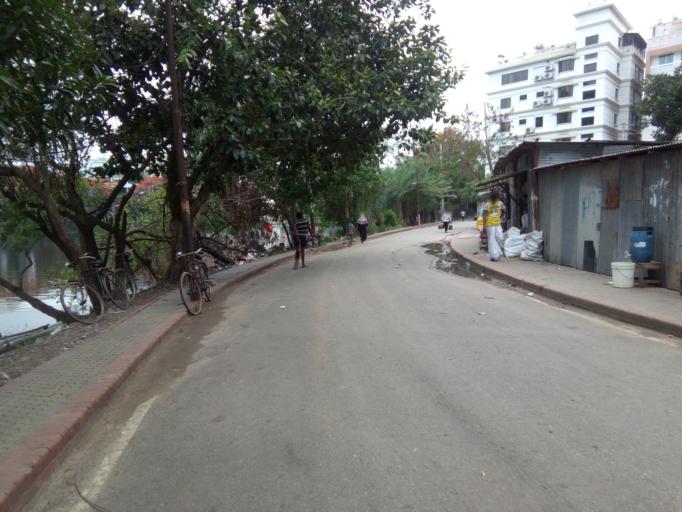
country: BD
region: Dhaka
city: Paltan
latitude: 23.7910
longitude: 90.4113
